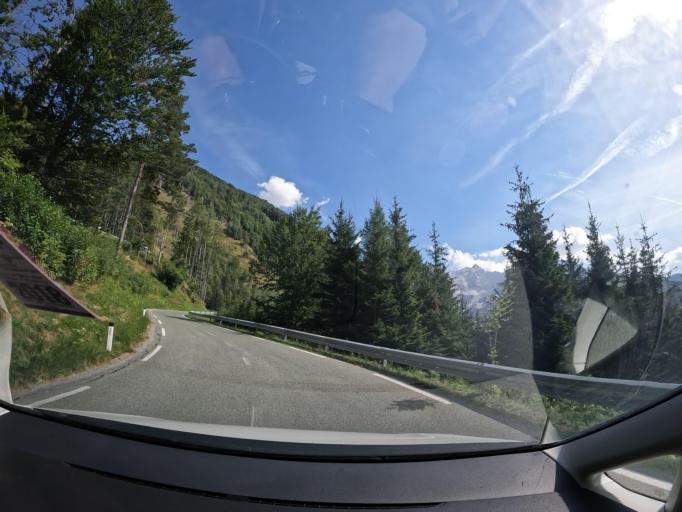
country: AT
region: Carinthia
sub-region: Politischer Bezirk Sankt Veit an der Glan
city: Liebenfels
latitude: 46.7071
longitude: 14.2796
